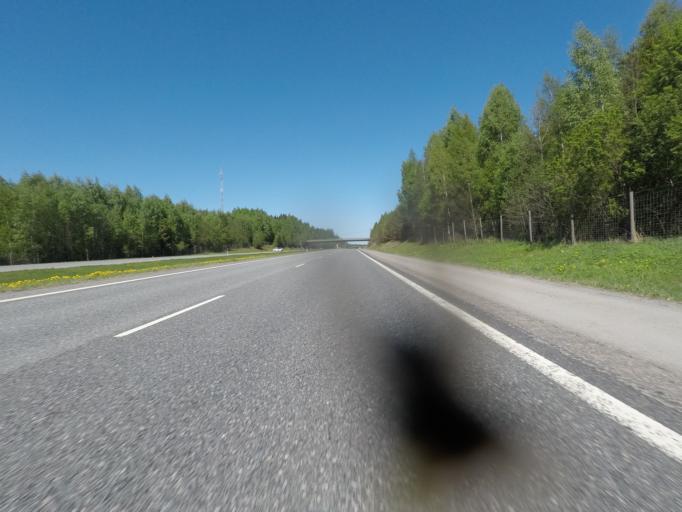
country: FI
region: Haeme
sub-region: Haemeenlinna
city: Janakkala
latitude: 60.8842
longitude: 24.5684
